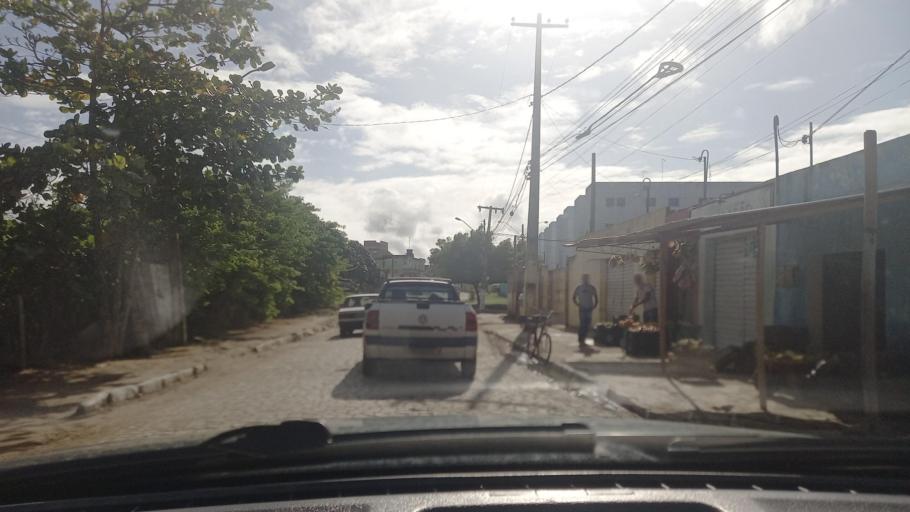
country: BR
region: Pernambuco
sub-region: Vitoria De Santo Antao
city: Vitoria de Santo Antao
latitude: -8.0983
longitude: -35.2785
